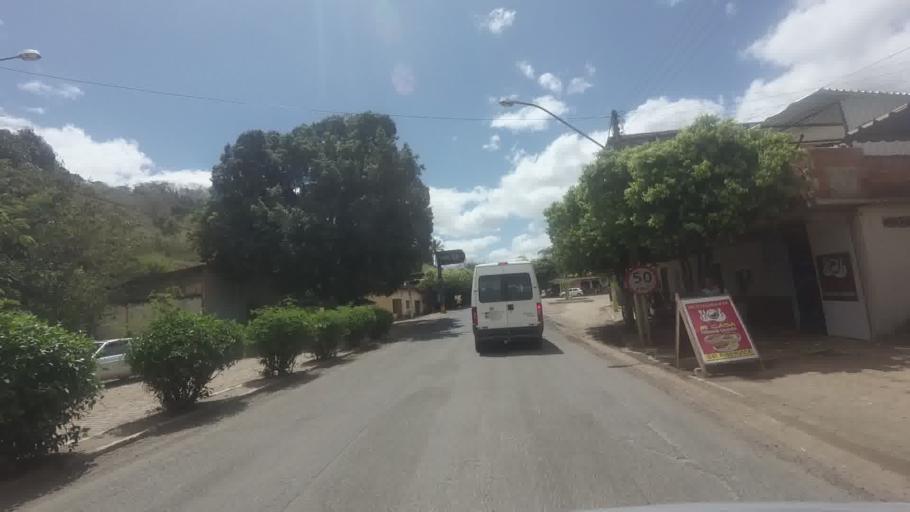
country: BR
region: Rio de Janeiro
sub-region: Santo Antonio De Padua
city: Santo Antonio de Padua
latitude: -21.5022
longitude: -42.0799
